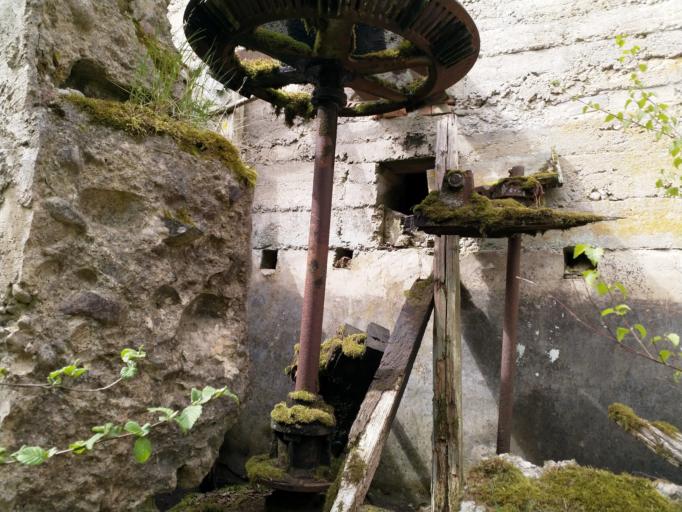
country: LV
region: Kuldigas Rajons
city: Kuldiga
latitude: 56.8502
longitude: 21.7797
